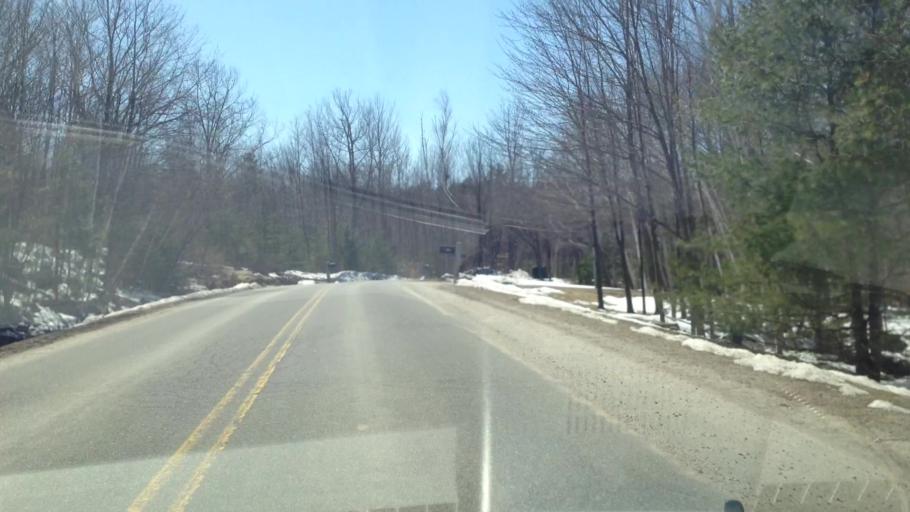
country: US
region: New Hampshire
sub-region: Hillsborough County
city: New Boston
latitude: 42.9919
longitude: -71.6557
